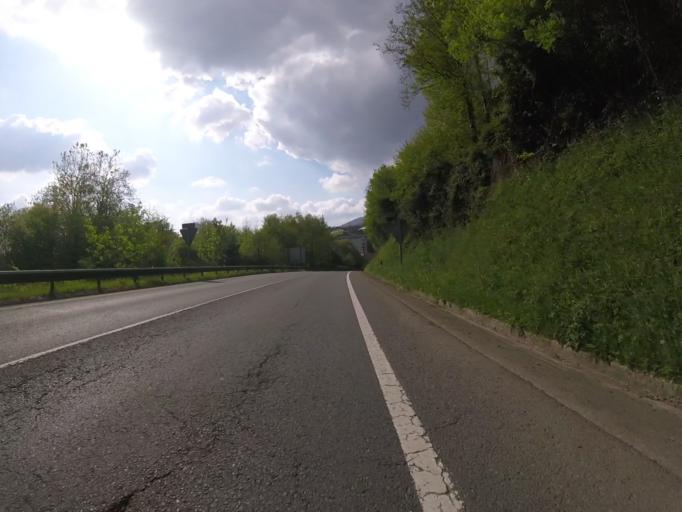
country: ES
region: Basque Country
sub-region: Provincia de Guipuzcoa
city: Azkoitia
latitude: 43.1781
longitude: -2.3174
